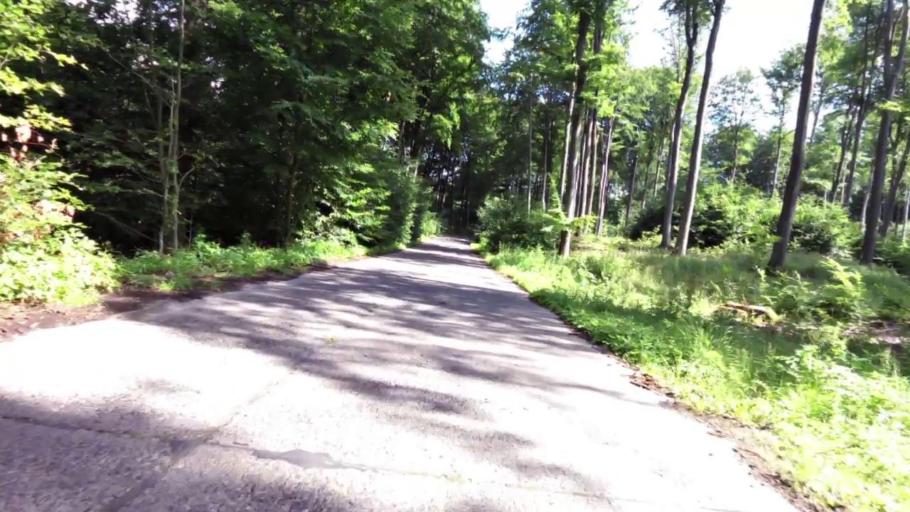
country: PL
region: West Pomeranian Voivodeship
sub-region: Powiat stargardzki
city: Dobrzany
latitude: 53.3911
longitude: 15.4729
